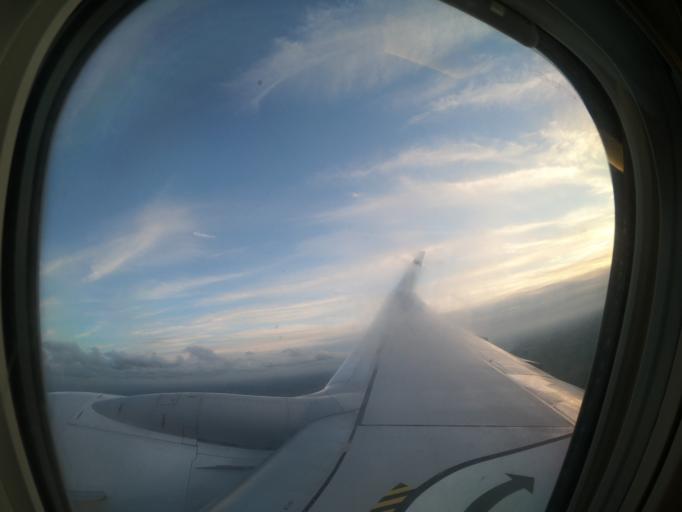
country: GB
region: England
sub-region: Essex
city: Hatfield Heath
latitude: 51.8225
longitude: 0.2120
